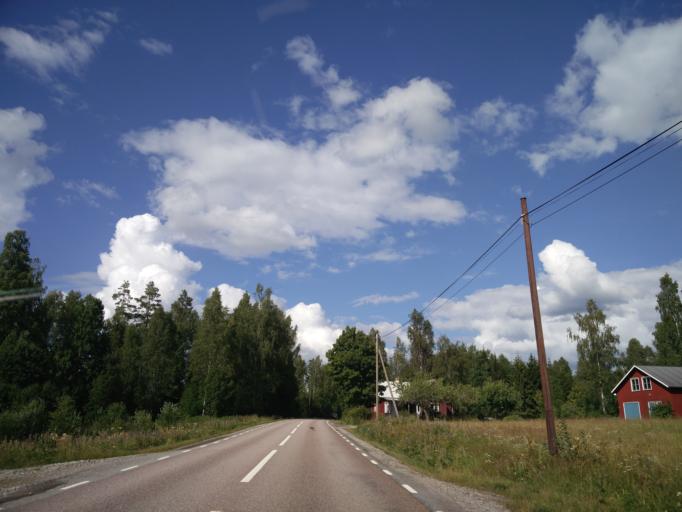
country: SE
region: Vaermland
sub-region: Sunne Kommun
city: Sunne
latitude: 59.6618
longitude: 12.9601
